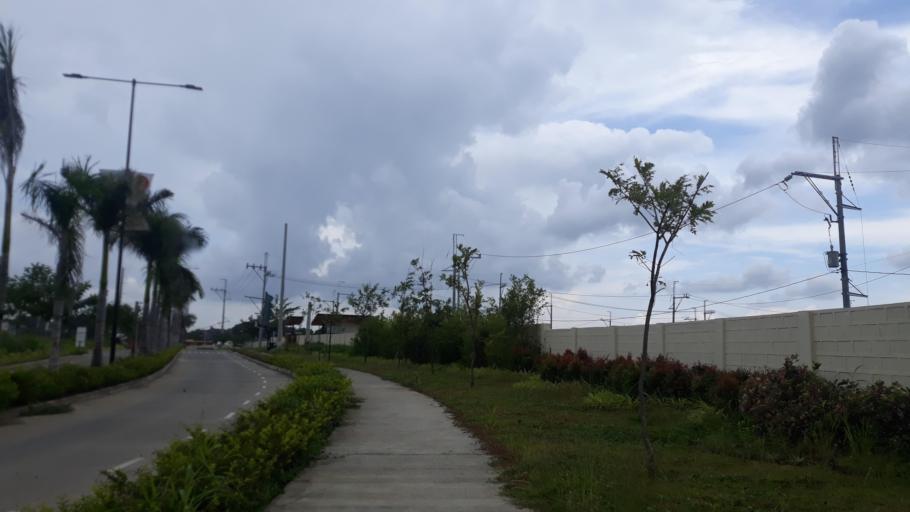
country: PH
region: Calabarzon
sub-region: Province of Cavite
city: Dasmarinas
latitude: 14.3041
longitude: 120.9493
